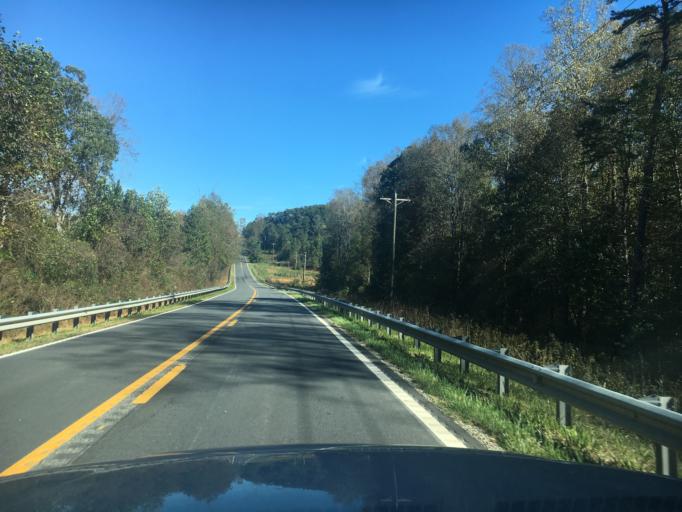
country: US
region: North Carolina
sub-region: Burke County
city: Glen Alpine
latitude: 35.6039
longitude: -81.8177
